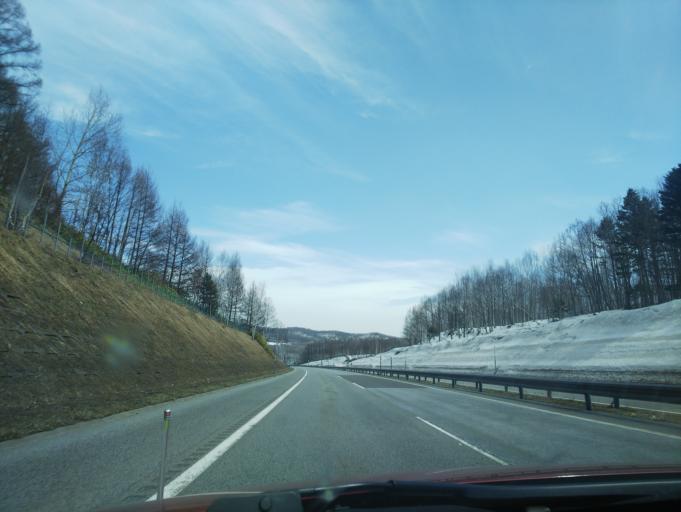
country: JP
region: Hokkaido
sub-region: Asahikawa-shi
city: Asahikawa
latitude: 43.7923
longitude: 142.2720
